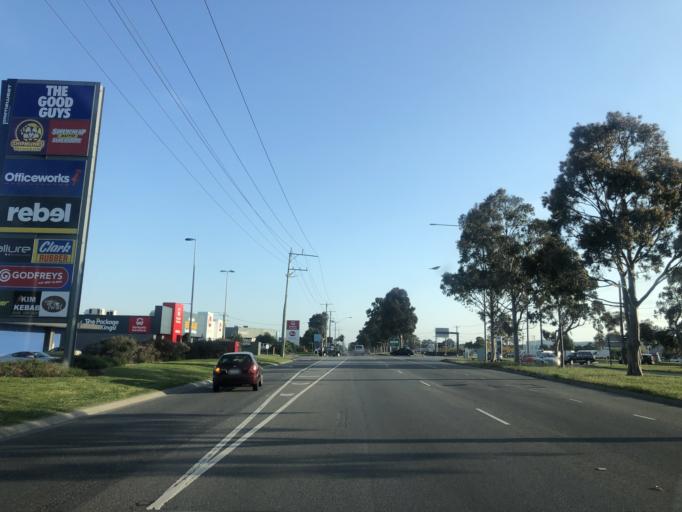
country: AU
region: Victoria
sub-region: Casey
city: Doveton
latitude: -38.0053
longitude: 145.2174
